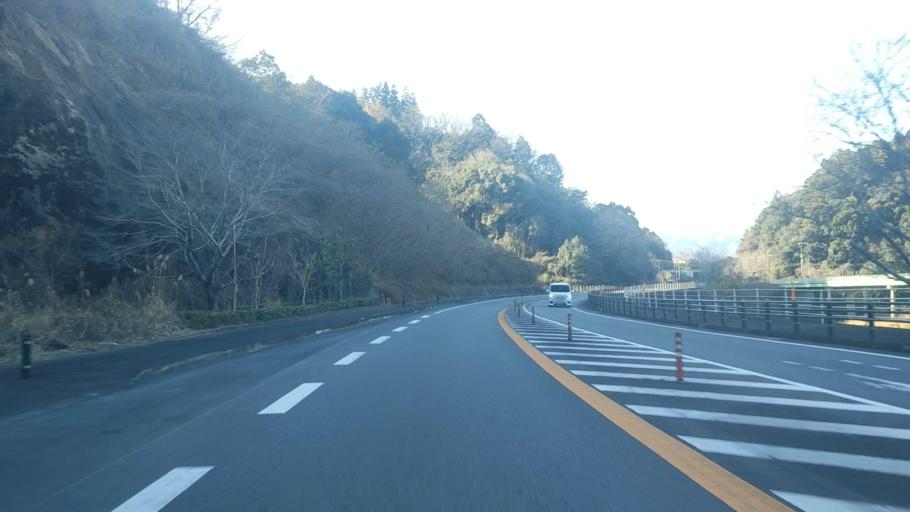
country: JP
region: Oita
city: Usuki
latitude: 33.0610
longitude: 131.6691
